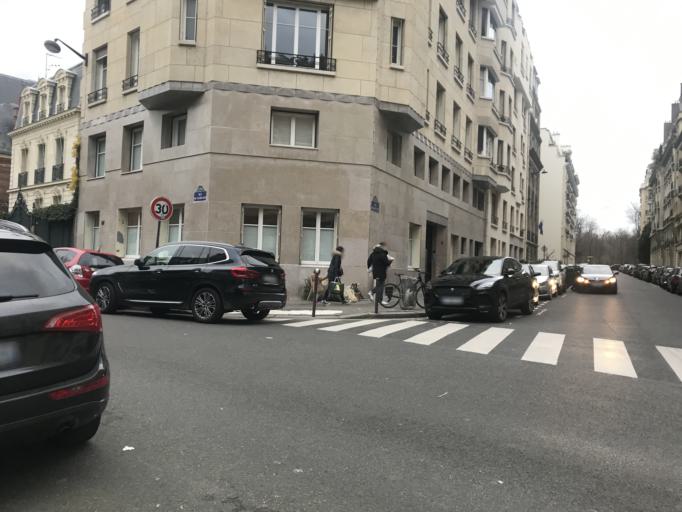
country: FR
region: Ile-de-France
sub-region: Departement des Hauts-de-Seine
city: Neuilly-sur-Seine
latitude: 48.8560
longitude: 2.2692
